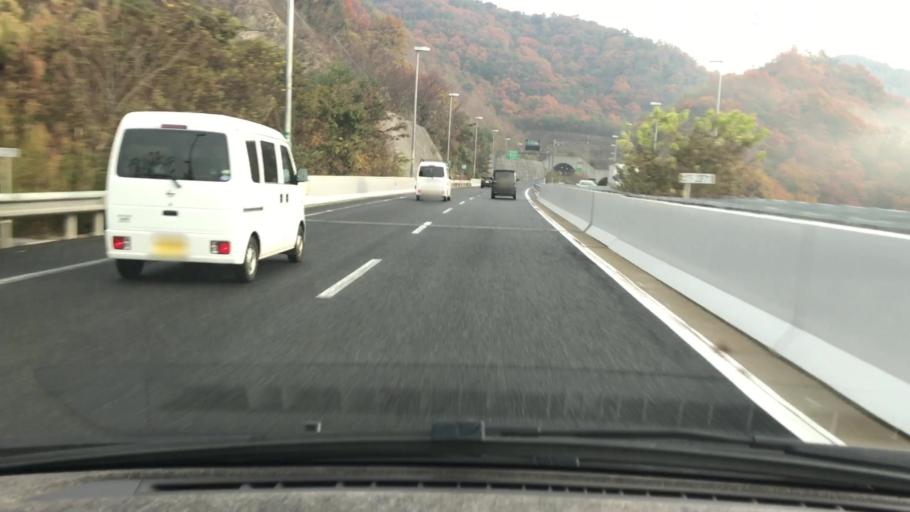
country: JP
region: Hyogo
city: Sandacho
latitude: 34.7977
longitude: 135.2297
